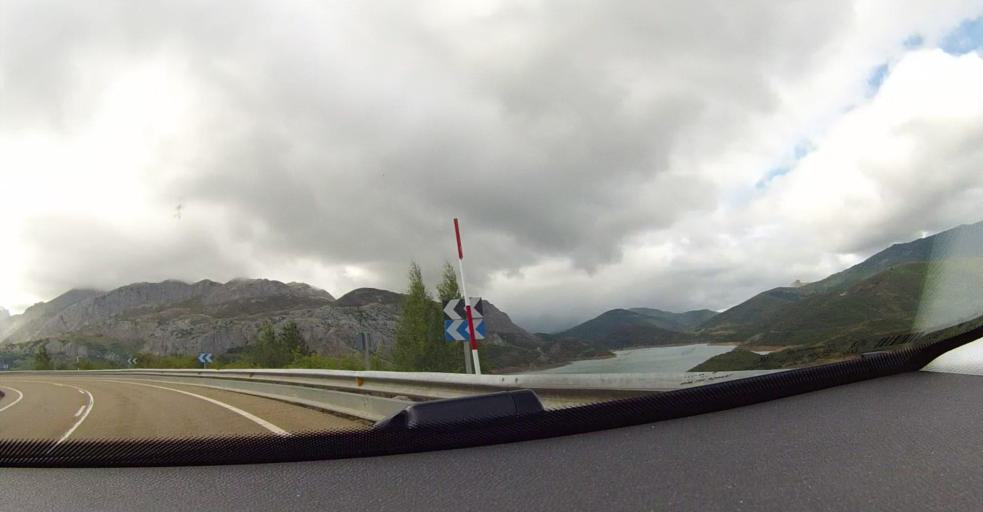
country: ES
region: Castille and Leon
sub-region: Provincia de Leon
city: Riano
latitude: 42.9790
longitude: -4.9981
